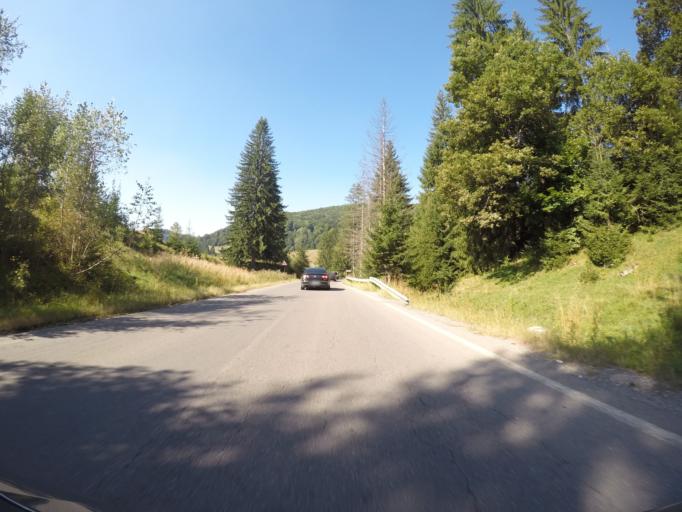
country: RO
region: Brasov
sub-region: Comuna Cristian
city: Cristian
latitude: 45.5933
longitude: 25.5281
